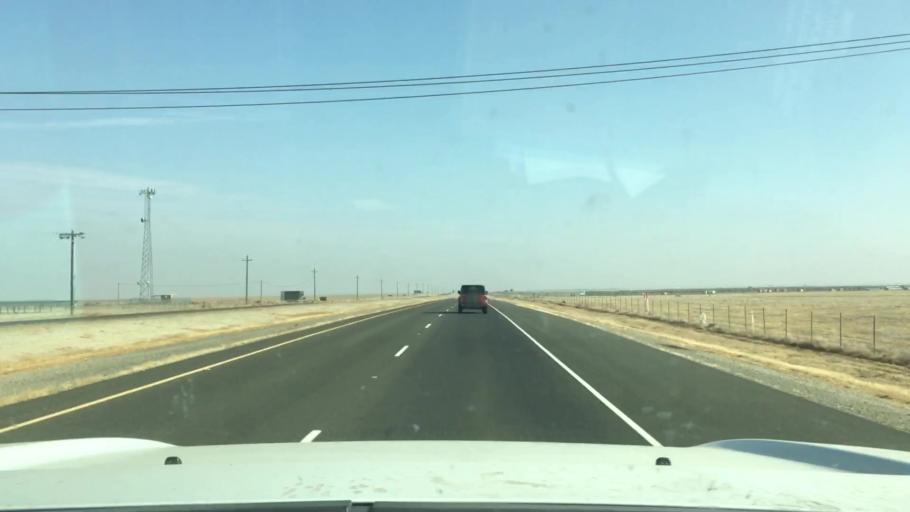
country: US
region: California
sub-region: Kern County
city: Lost Hills
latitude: 35.6151
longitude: -119.8531
